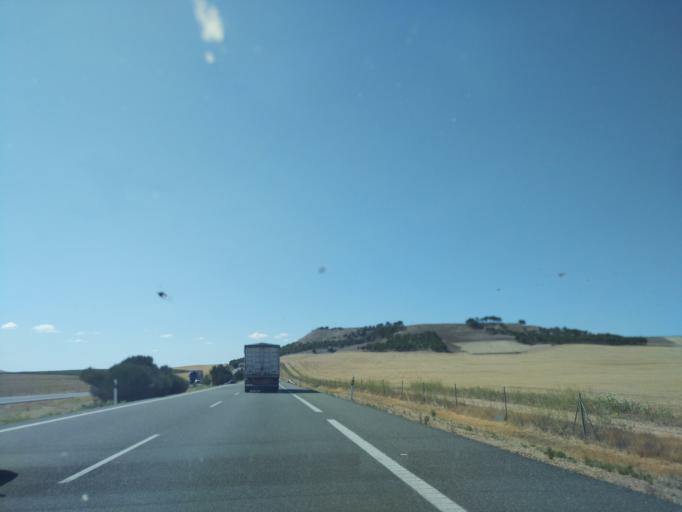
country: ES
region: Castille and Leon
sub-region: Provincia de Valladolid
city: Marzales
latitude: 41.6051
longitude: -5.1368
